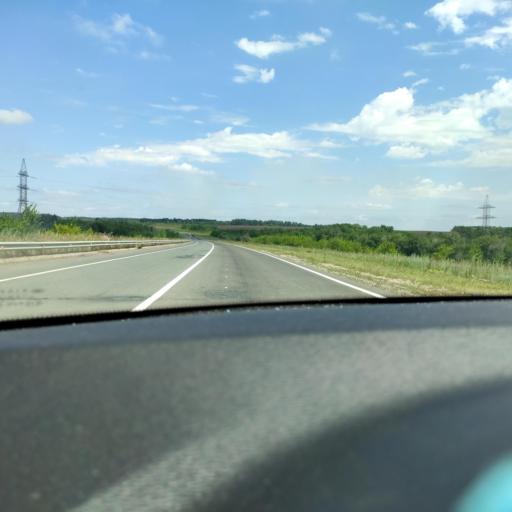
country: RU
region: Samara
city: Petra-Dubrava
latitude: 53.3056
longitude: 50.4168
